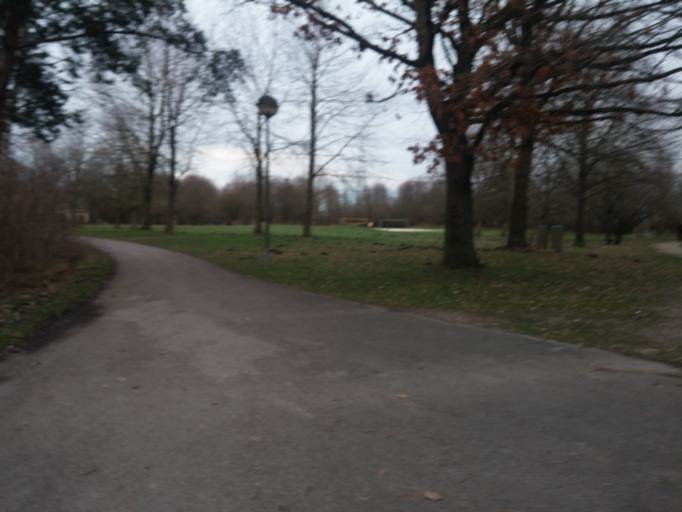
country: DE
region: Bavaria
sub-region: Upper Bavaria
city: Unterfoehring
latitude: 48.1908
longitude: 11.6723
